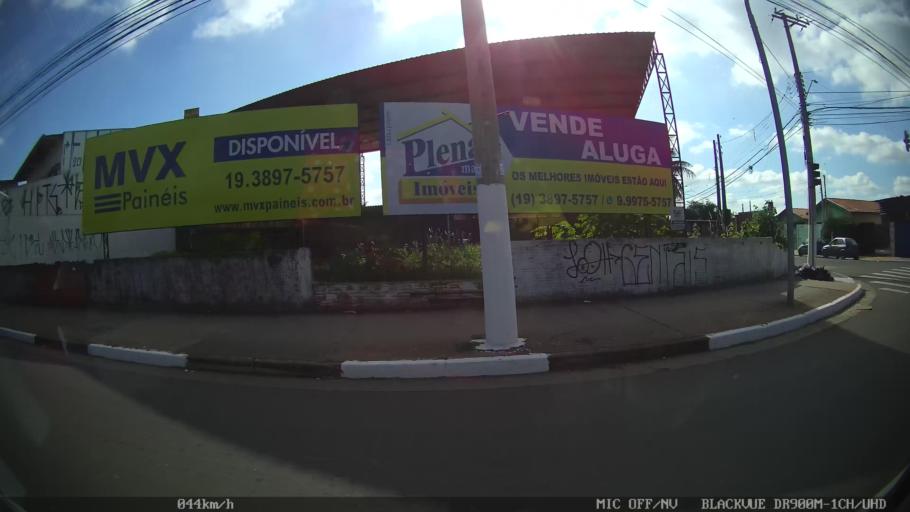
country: BR
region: Sao Paulo
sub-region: Hortolandia
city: Hortolandia
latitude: -22.8750
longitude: -47.2058
